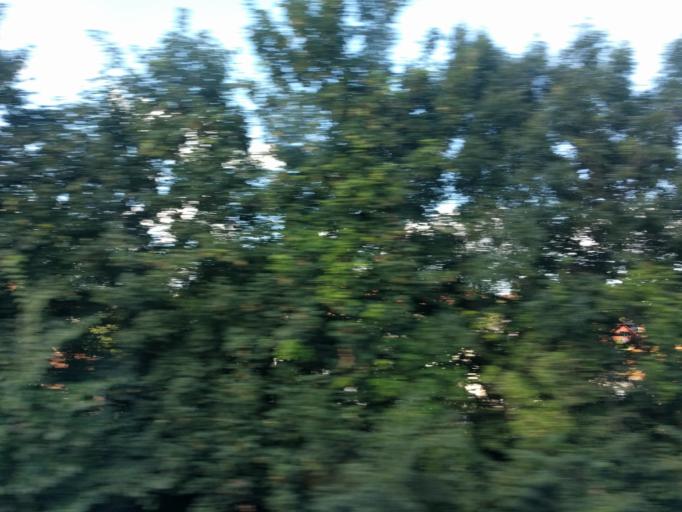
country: DK
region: Zealand
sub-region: Roskilde Kommune
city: Roskilde
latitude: 55.6323
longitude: 12.0742
